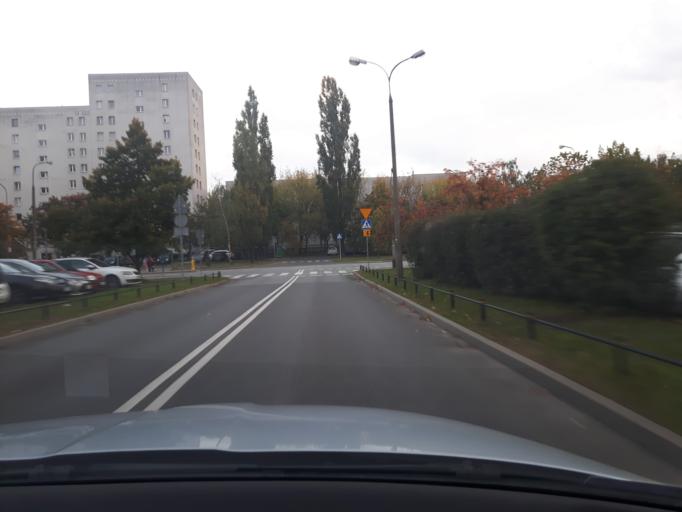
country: PL
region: Masovian Voivodeship
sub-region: Warszawa
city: Ursynow
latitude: 52.1390
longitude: 21.0528
